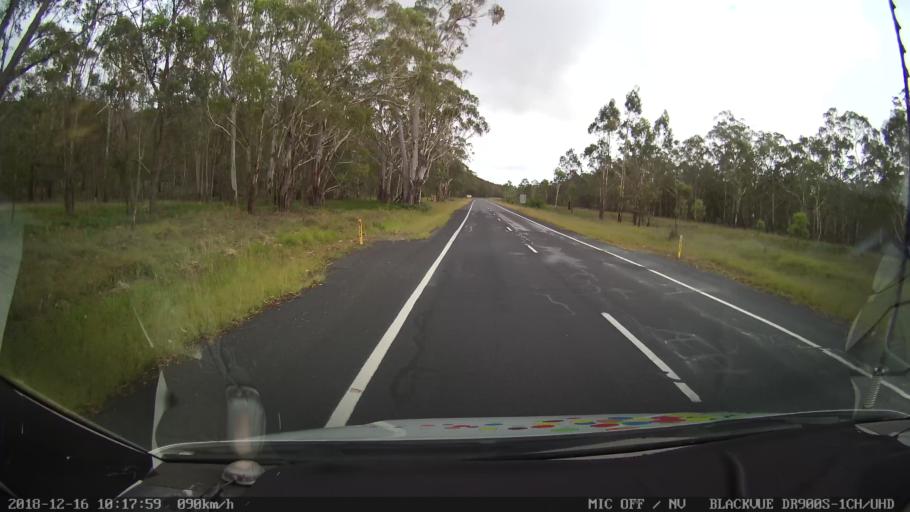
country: AU
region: New South Wales
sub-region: Tenterfield Municipality
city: Carrolls Creek
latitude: -29.2499
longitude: 151.9955
